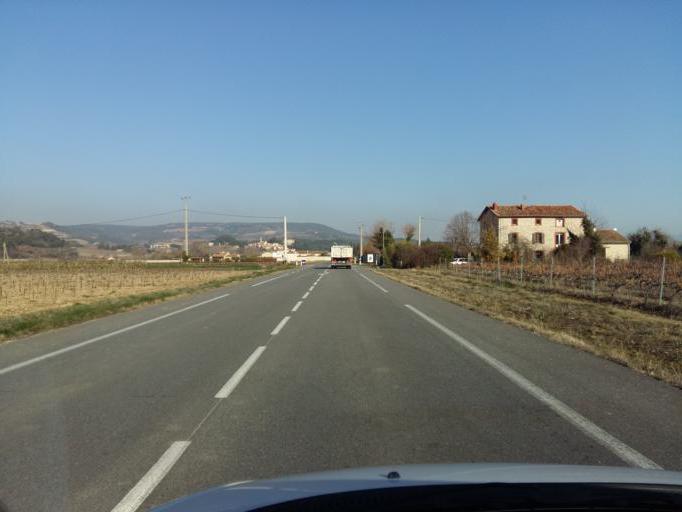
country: FR
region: Provence-Alpes-Cote d'Azur
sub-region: Departement du Vaucluse
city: Sablet
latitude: 44.2352
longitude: 5.0168
